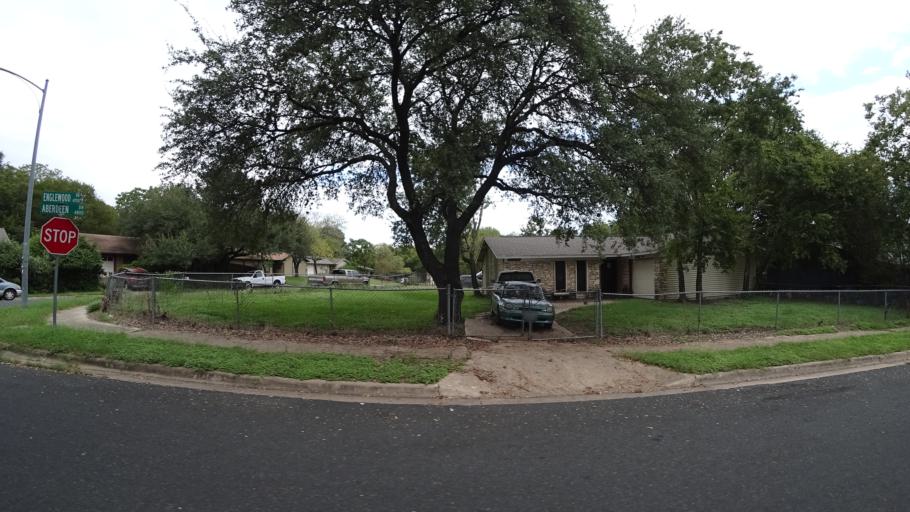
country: US
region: Texas
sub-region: Travis County
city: Rollingwood
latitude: 30.2169
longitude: -97.7800
